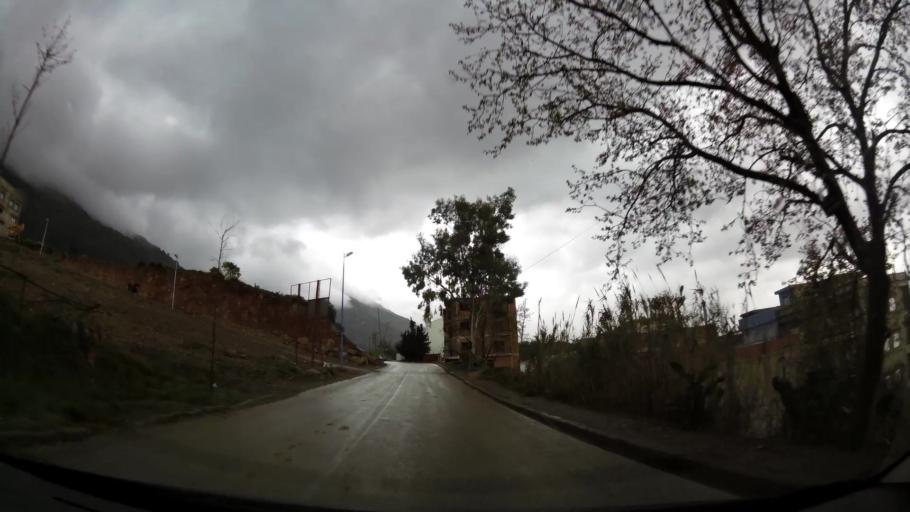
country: MA
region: Tanger-Tetouan
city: Chefchaouene
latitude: 35.1757
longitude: -5.2703
